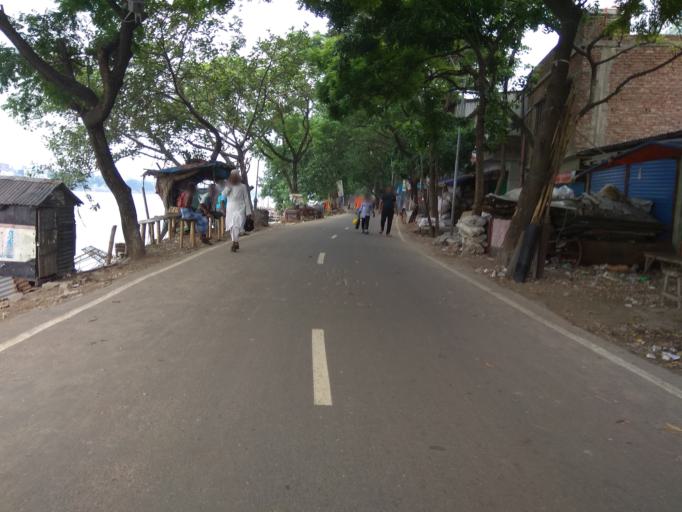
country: BD
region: Dhaka
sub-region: Dhaka
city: Dhaka
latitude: 23.7099
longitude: 90.3894
